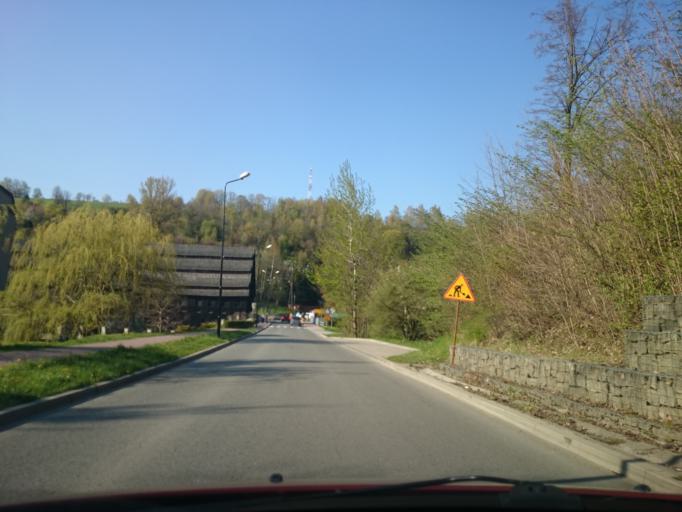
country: PL
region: Lower Silesian Voivodeship
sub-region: Powiat klodzki
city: Duszniki-Zdroj
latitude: 50.4035
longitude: 16.3958
